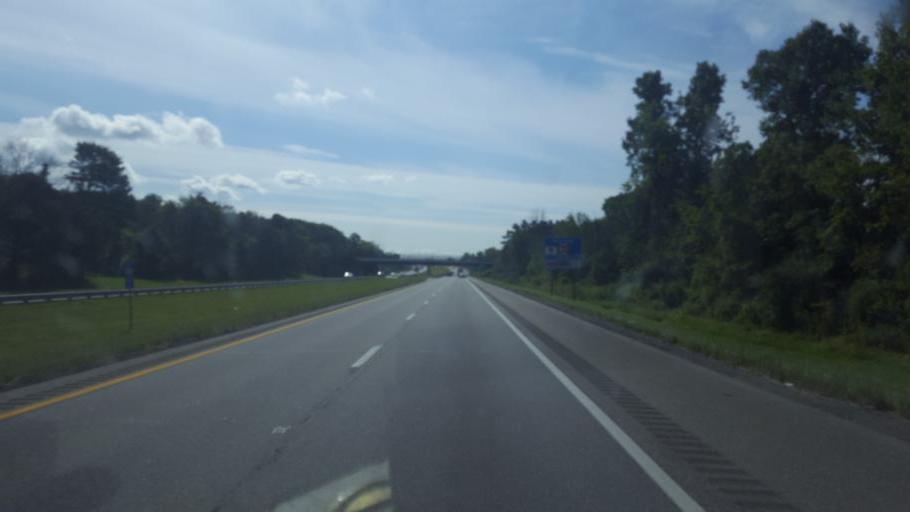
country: US
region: Ohio
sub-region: Cuyahoga County
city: Orange
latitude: 41.4152
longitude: -81.4742
